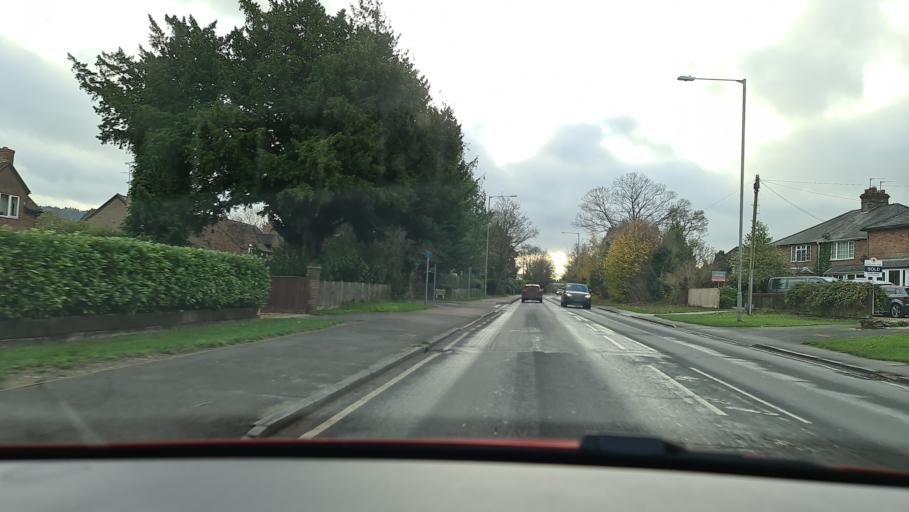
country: GB
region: England
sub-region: Buckinghamshire
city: Wendover
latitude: 51.7703
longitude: -0.7470
